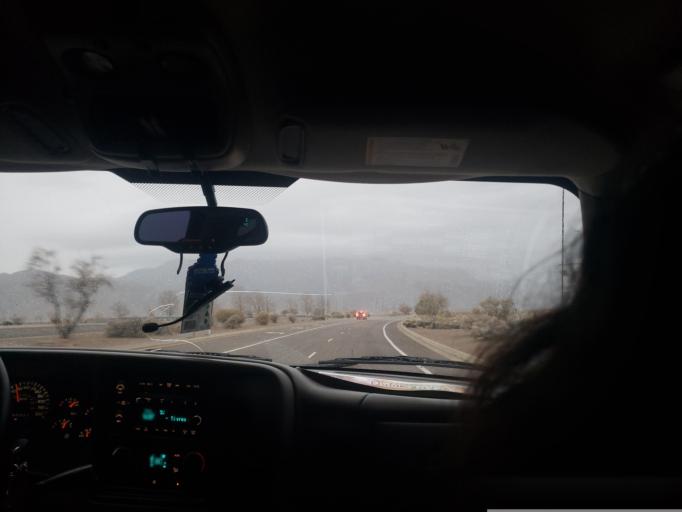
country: US
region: New Mexico
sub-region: Sandoval County
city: Corrales
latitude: 35.2023
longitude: -106.5628
